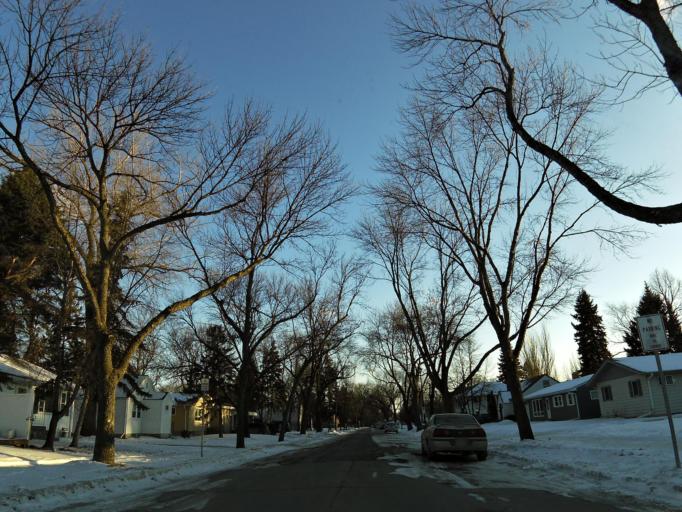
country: US
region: North Dakota
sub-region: Grand Forks County
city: Grand Forks
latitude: 47.9257
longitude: -97.0706
